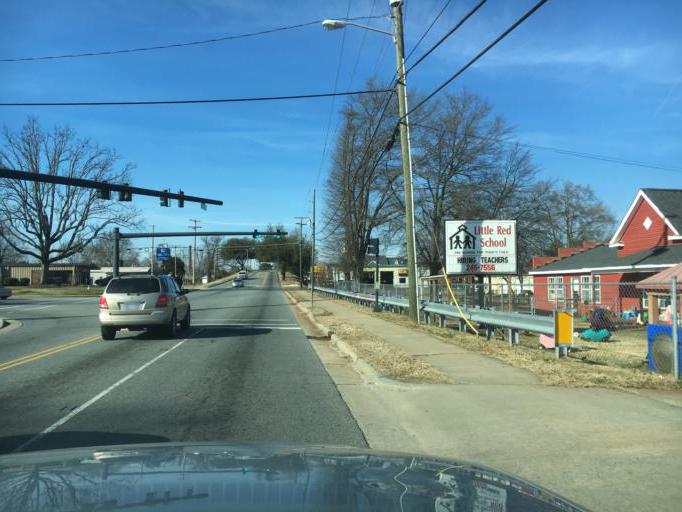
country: US
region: North Carolina
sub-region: Rutherford County
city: Forest City
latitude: 35.3270
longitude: -81.8618
